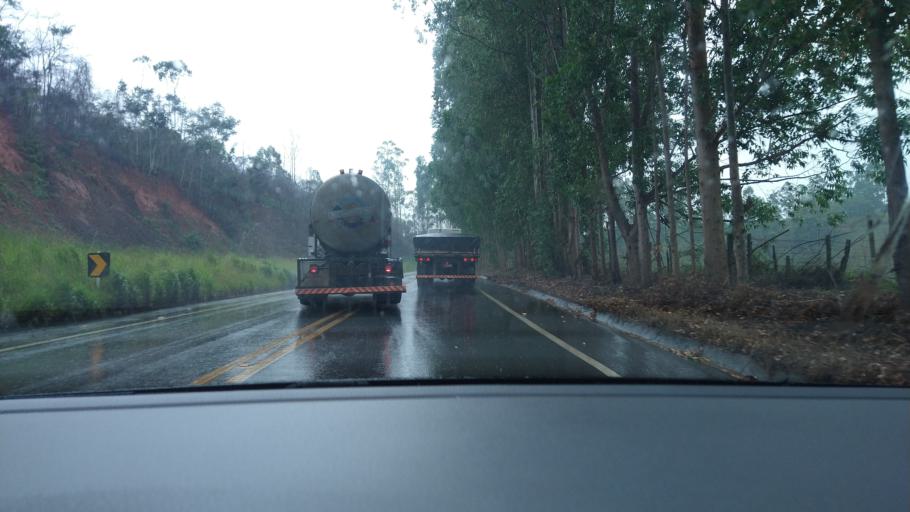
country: BR
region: Minas Gerais
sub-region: Ponte Nova
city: Ponte Nova
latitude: -20.5796
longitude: -42.8809
